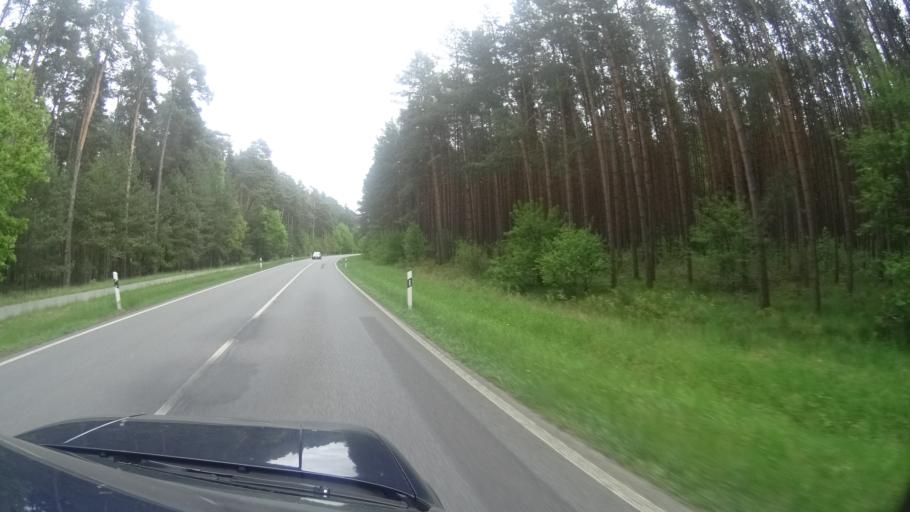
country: DE
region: Mecklenburg-Vorpommern
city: Malchow
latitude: 53.4602
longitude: 12.4070
